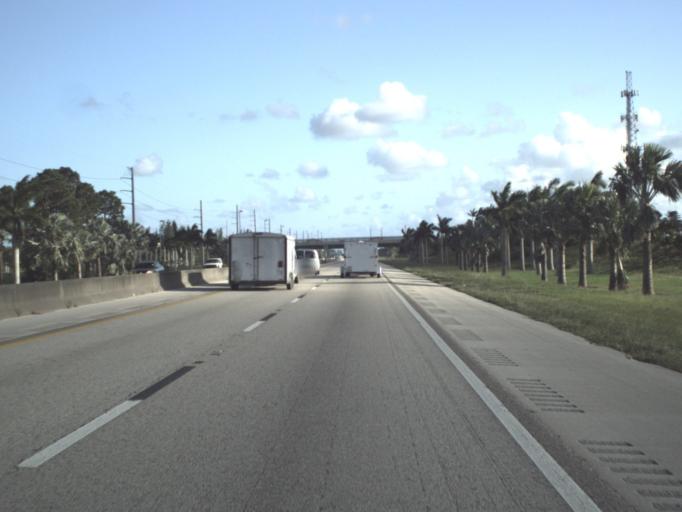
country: US
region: Florida
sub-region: Martin County
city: North River Shores
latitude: 27.2131
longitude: -80.3354
